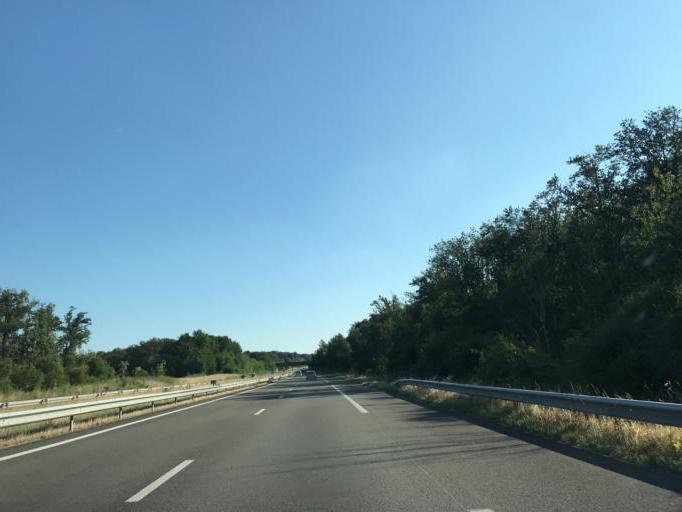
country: FR
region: Rhone-Alpes
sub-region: Departement de l'Ain
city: Marboz
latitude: 46.3214
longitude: 5.2684
